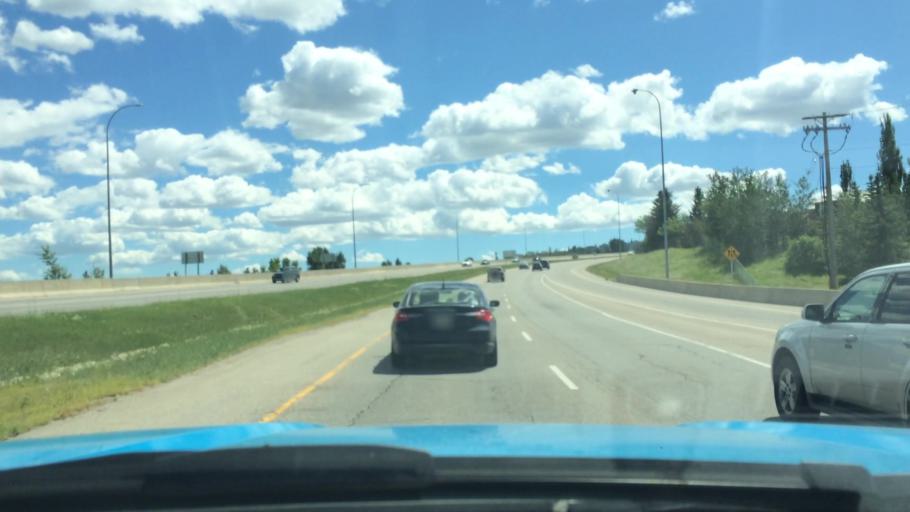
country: CA
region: Alberta
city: Calgary
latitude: 51.1408
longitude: -114.1221
